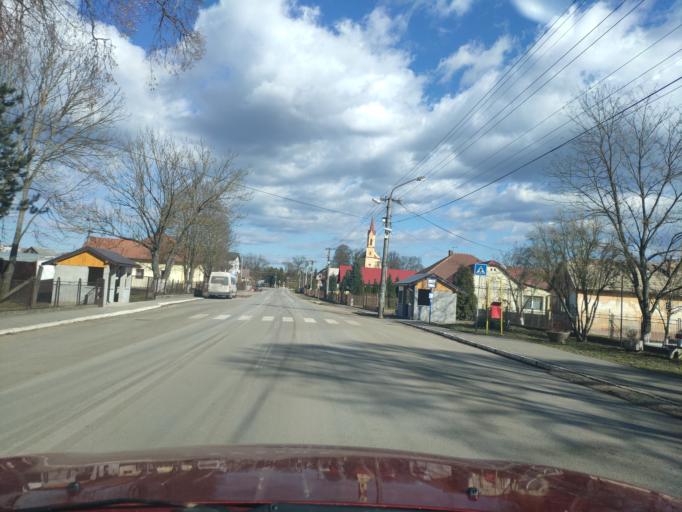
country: HU
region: Borsod-Abauj-Zemplen
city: Putnok
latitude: 48.3184
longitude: 20.3358
